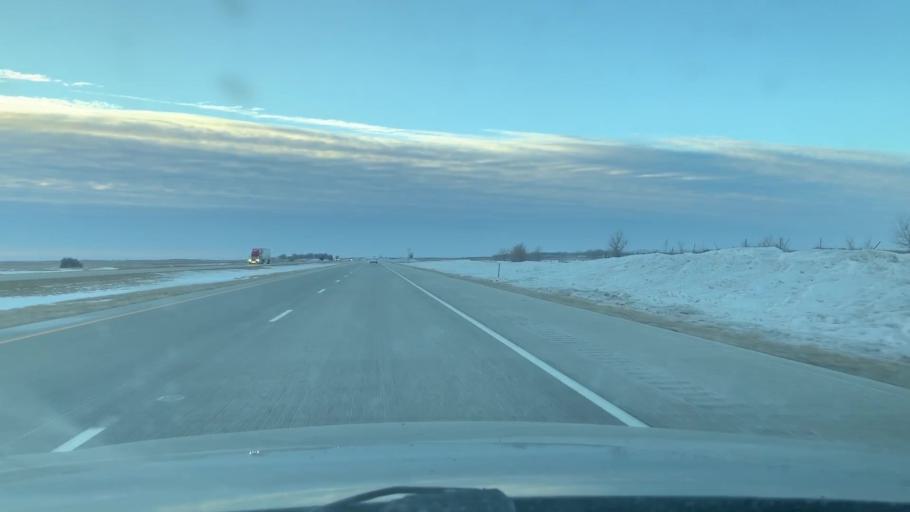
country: US
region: North Dakota
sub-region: Ransom County
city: Sheldon
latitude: 46.8759
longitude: -97.5045
